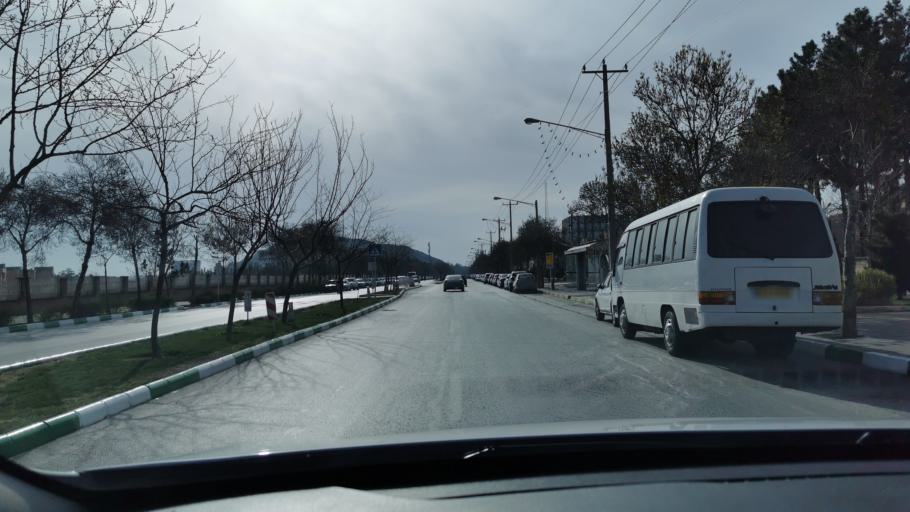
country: IR
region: Razavi Khorasan
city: Mashhad
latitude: 36.2838
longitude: 59.5497
